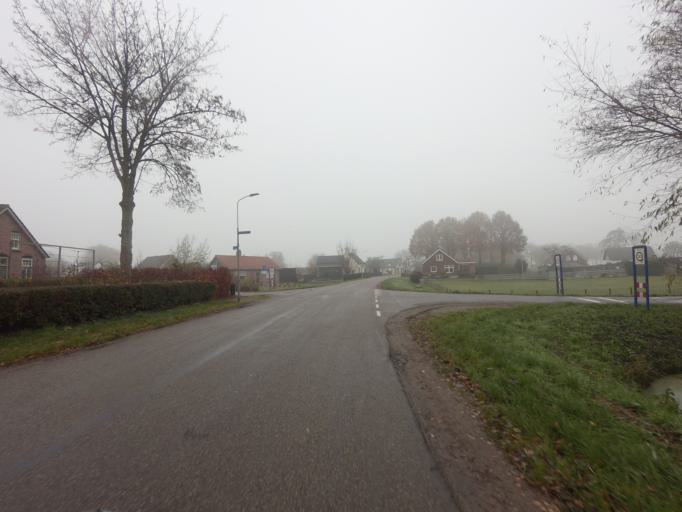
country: NL
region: Gelderland
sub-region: Gemeente Zaltbommel
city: Nederhemert-Noord
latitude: 51.7698
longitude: 5.1876
